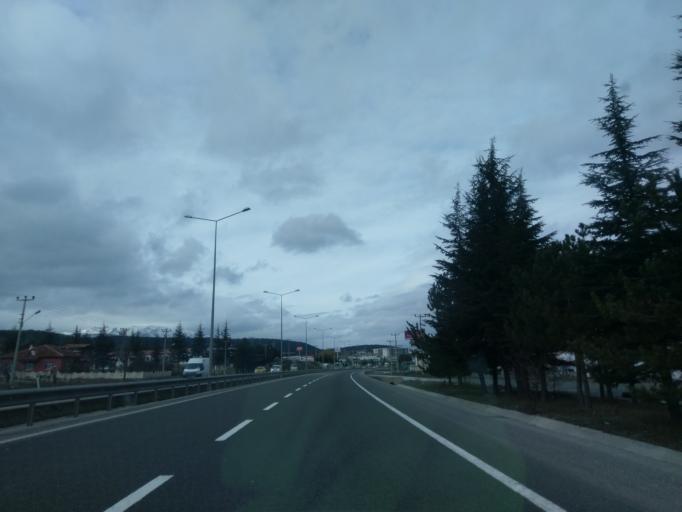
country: TR
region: Kuetahya
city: Kutahya
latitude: 39.3770
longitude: 30.0536
